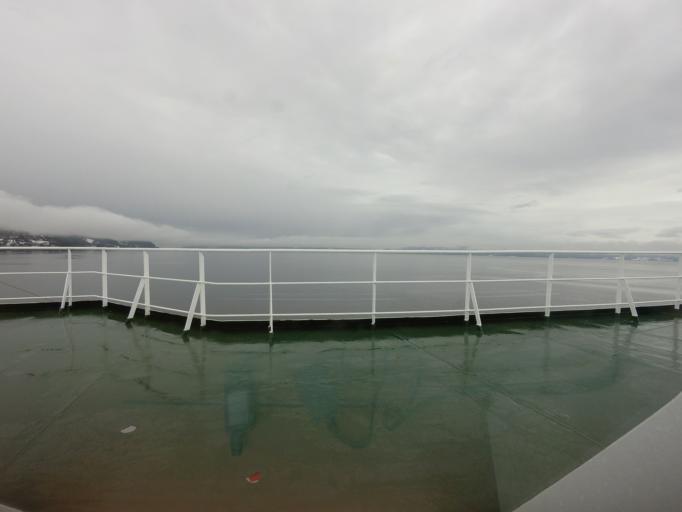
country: NO
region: Sor-Trondelag
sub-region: Trondheim
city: Trondheim
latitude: 63.4468
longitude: 10.3723
